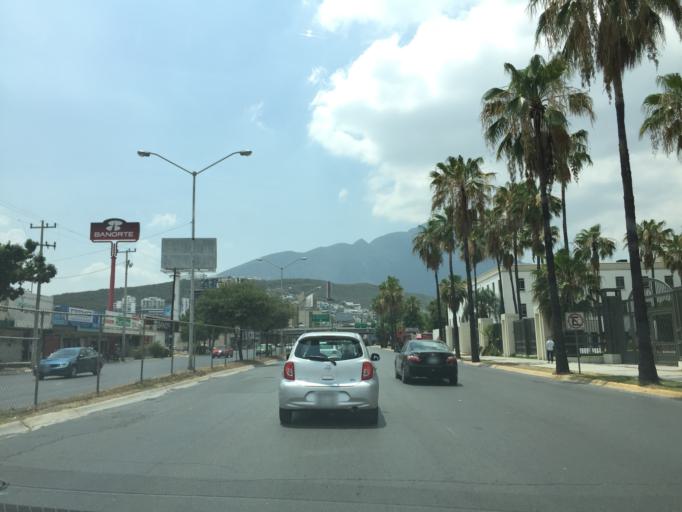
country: MX
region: Nuevo Leon
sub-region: Monterrey
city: Monterrey
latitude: 25.6879
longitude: -100.3494
